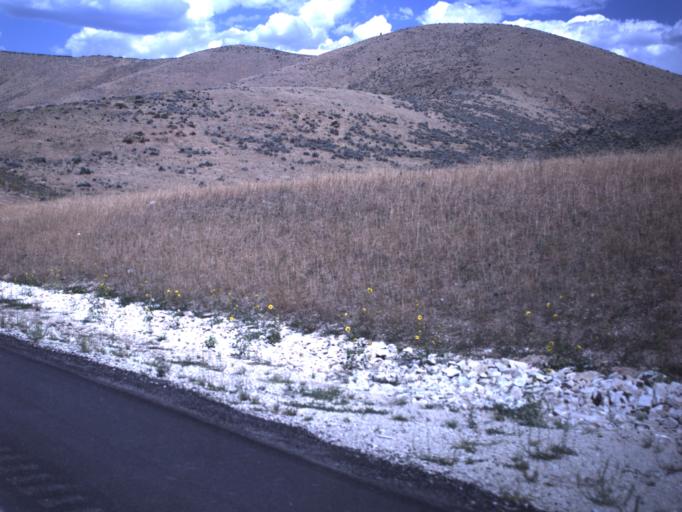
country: US
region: Utah
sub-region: Wasatch County
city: Midway
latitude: 40.4218
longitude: -111.4895
